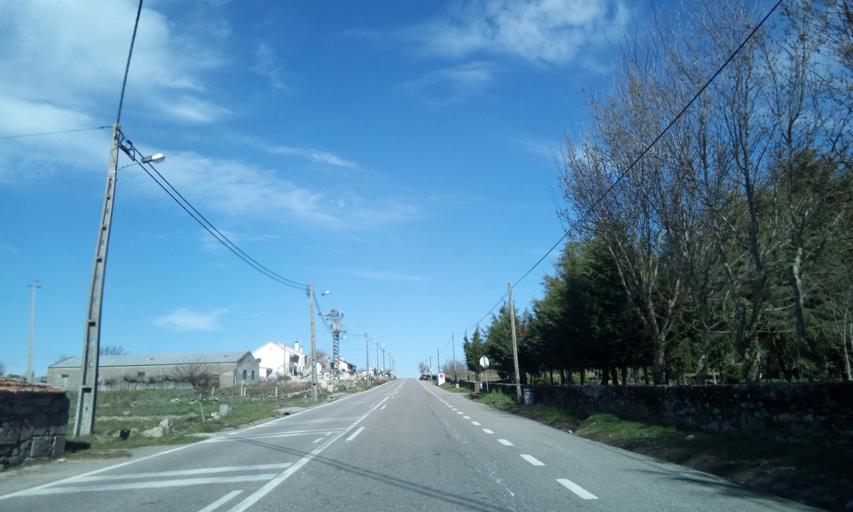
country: PT
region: Guarda
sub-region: Guarda
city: Sequeira
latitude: 40.5912
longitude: -7.1407
